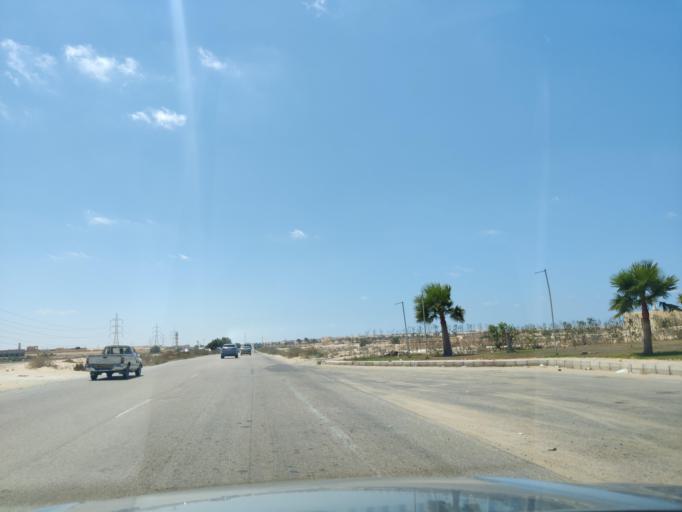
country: EG
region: Muhafazat Matruh
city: Al `Alamayn
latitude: 31.0686
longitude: 28.1684
